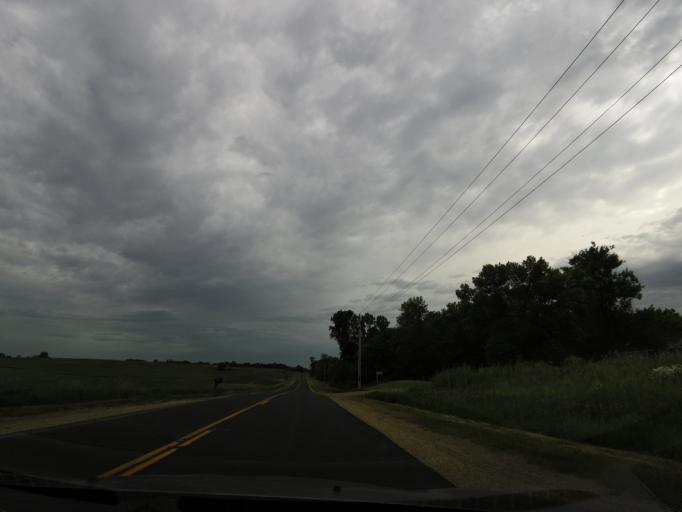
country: US
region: Minnesota
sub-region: Scott County
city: Prior Lake
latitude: 44.6754
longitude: -93.4197
